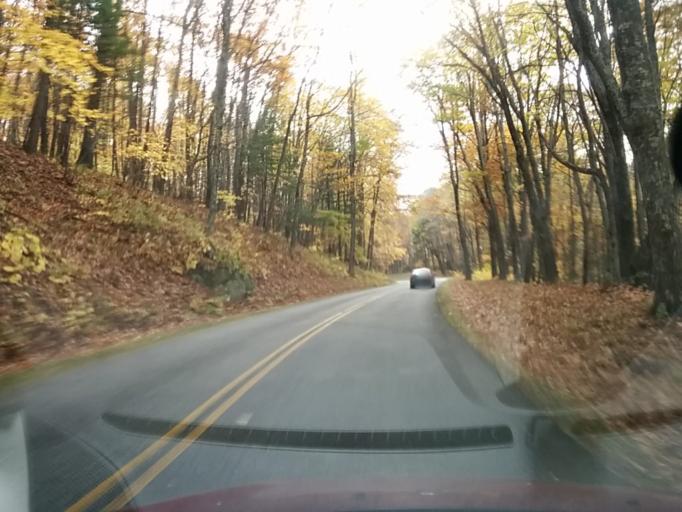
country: US
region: Virginia
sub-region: City of Buena Vista
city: Buena Vista
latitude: 37.8121
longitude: -79.1780
